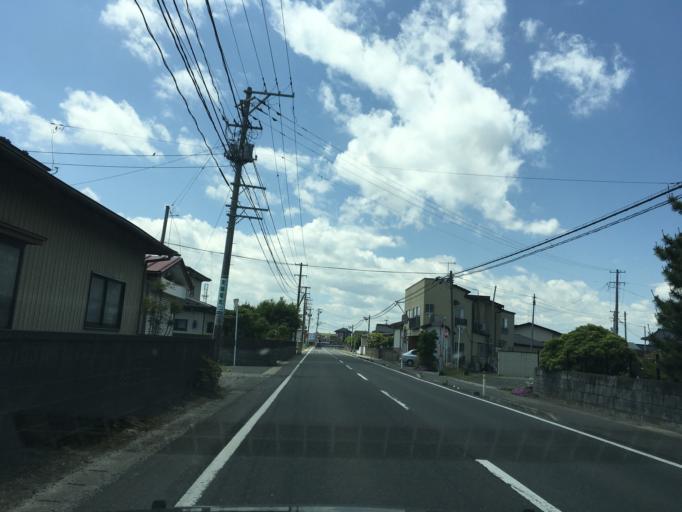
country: JP
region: Miyagi
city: Wakuya
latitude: 38.6791
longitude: 141.2161
